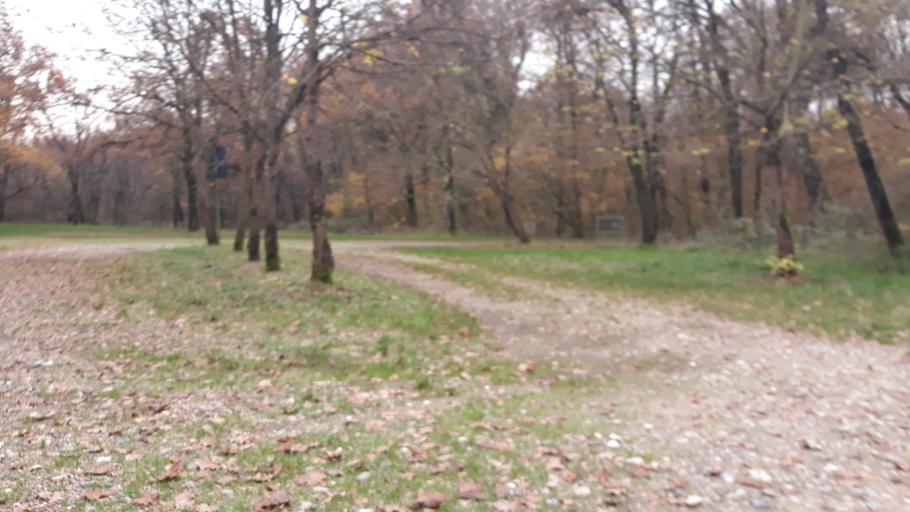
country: IT
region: Lombardy
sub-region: Citta metropolitana di Milano
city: Nosate
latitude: 45.5443
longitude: 8.7077
